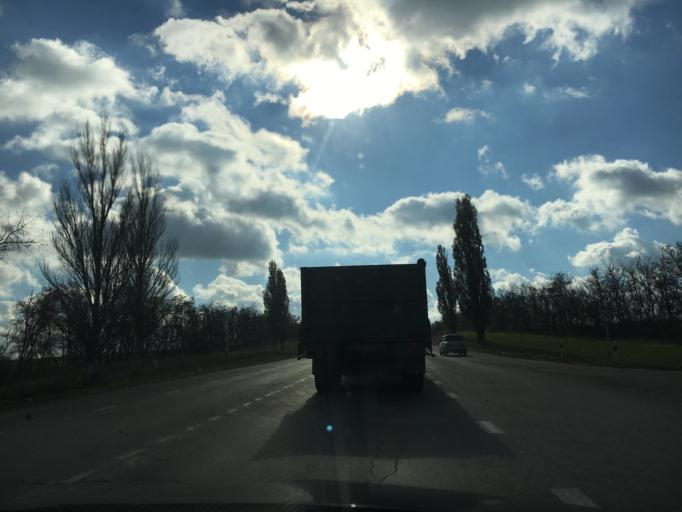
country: RU
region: Rostov
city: Matveyev Kurgan
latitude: 47.5448
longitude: 38.8909
